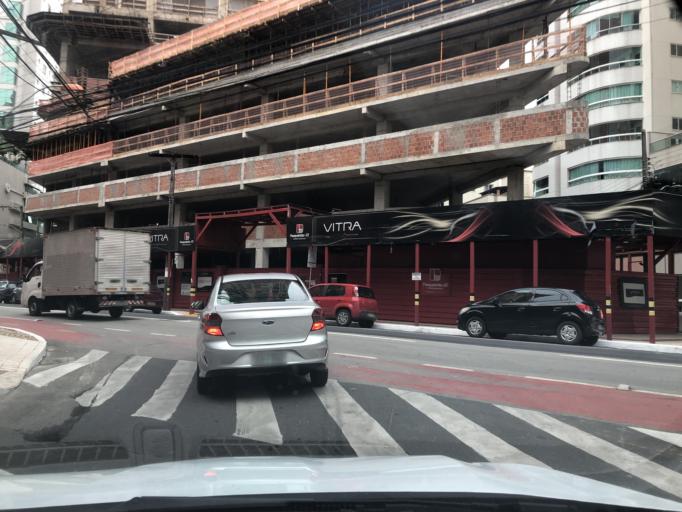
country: BR
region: Santa Catarina
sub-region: Balneario Camboriu
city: Balneario Camboriu
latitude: -27.0013
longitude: -48.6234
